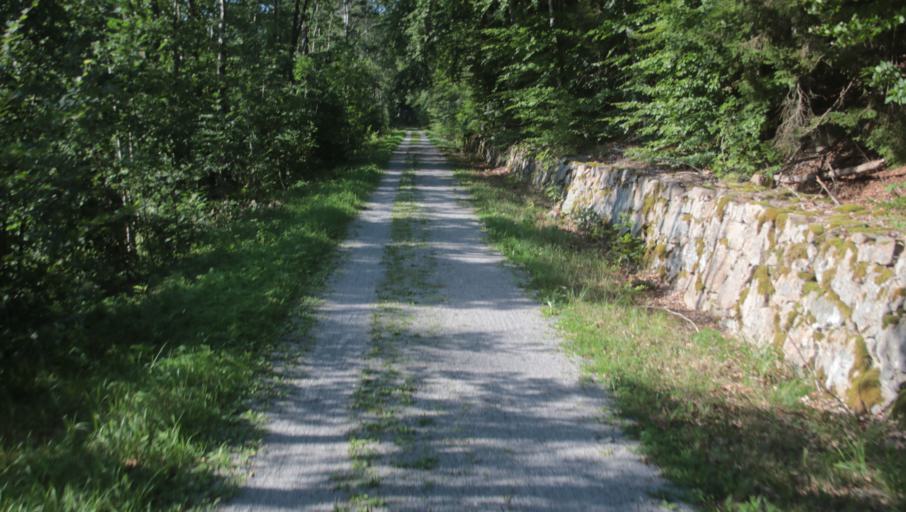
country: SE
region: Blekinge
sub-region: Karlshamns Kommun
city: Svangsta
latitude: 56.3587
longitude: 14.6906
